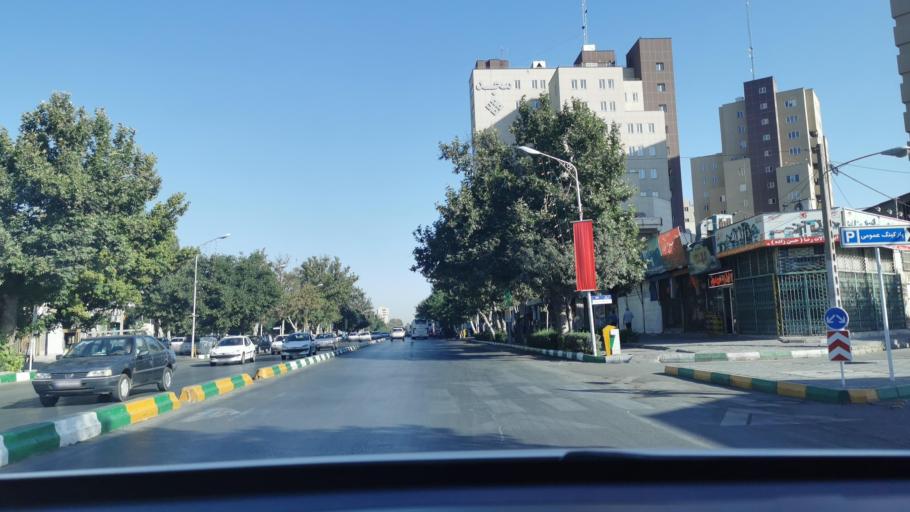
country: IR
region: Razavi Khorasan
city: Mashhad
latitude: 36.3110
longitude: 59.5919
